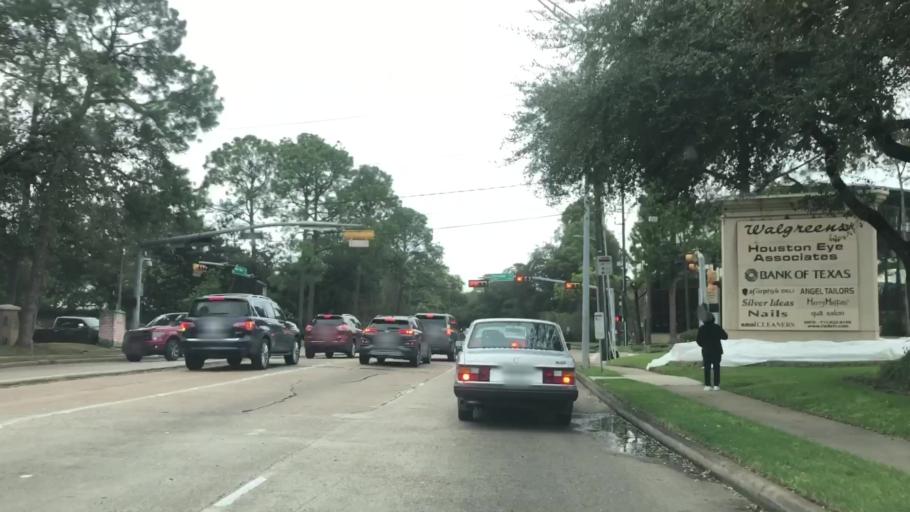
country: US
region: Texas
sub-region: Harris County
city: Hunters Creek Village
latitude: 29.7644
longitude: -95.4782
